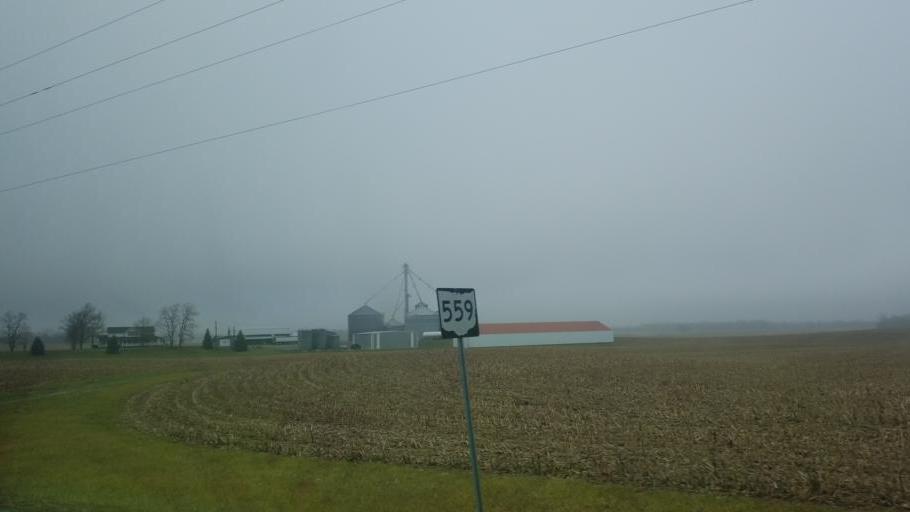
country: US
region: Ohio
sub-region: Champaign County
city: North Lewisburg
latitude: 40.2554
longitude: -83.5815
